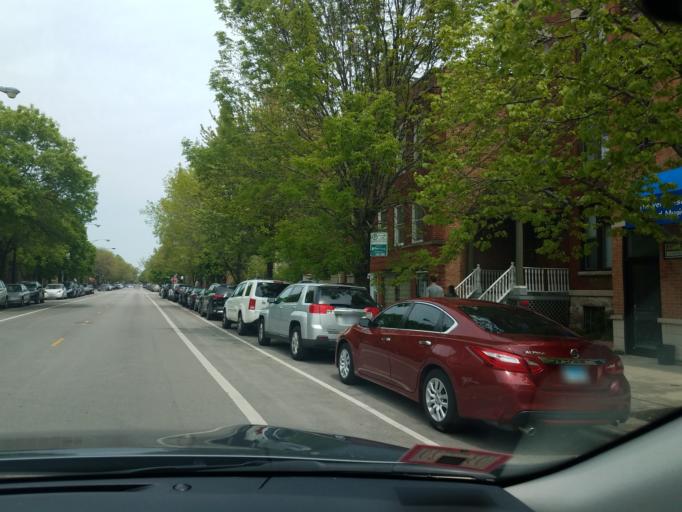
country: US
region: Illinois
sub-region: Cook County
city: Lincolnwood
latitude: 41.9515
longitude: -87.6641
